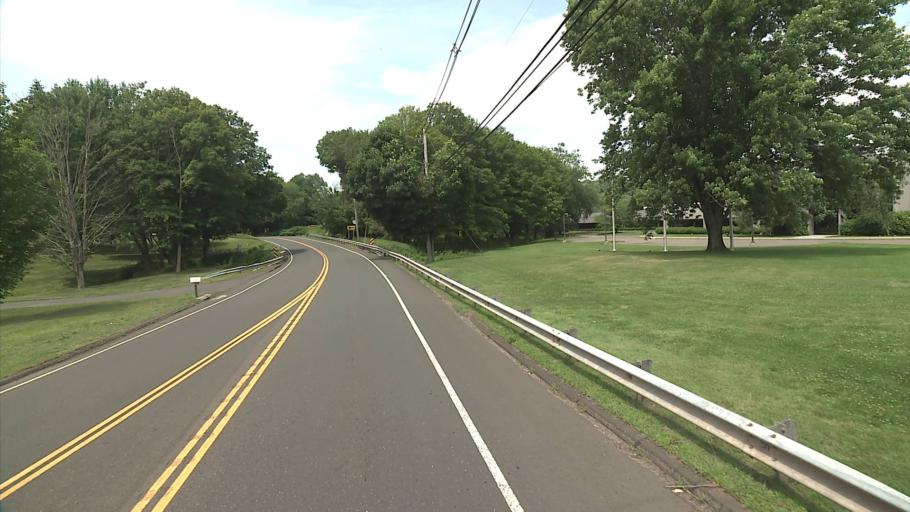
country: US
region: Connecticut
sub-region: New Haven County
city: North Haven
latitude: 41.3944
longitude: -72.8158
